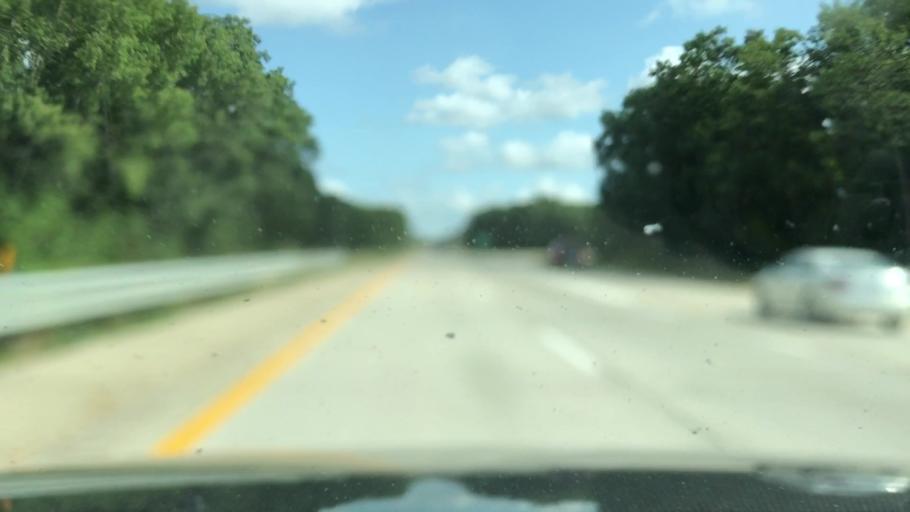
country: US
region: Michigan
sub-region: Montcalm County
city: Howard City
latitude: 43.3906
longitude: -85.5154
